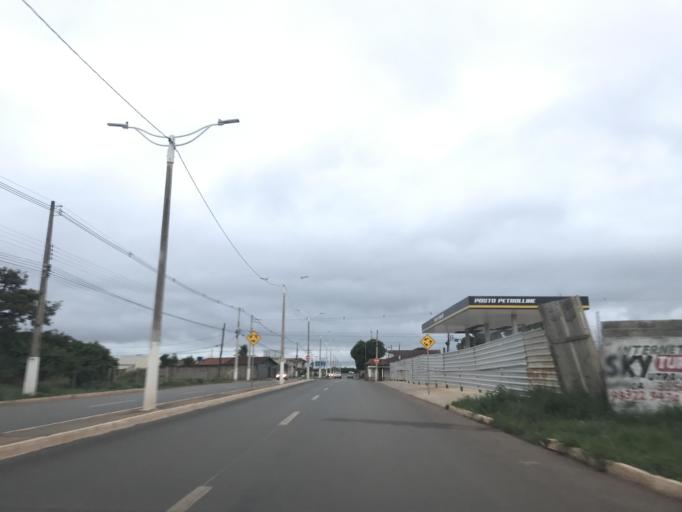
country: BR
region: Goias
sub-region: Luziania
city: Luziania
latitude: -16.2035
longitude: -47.9239
